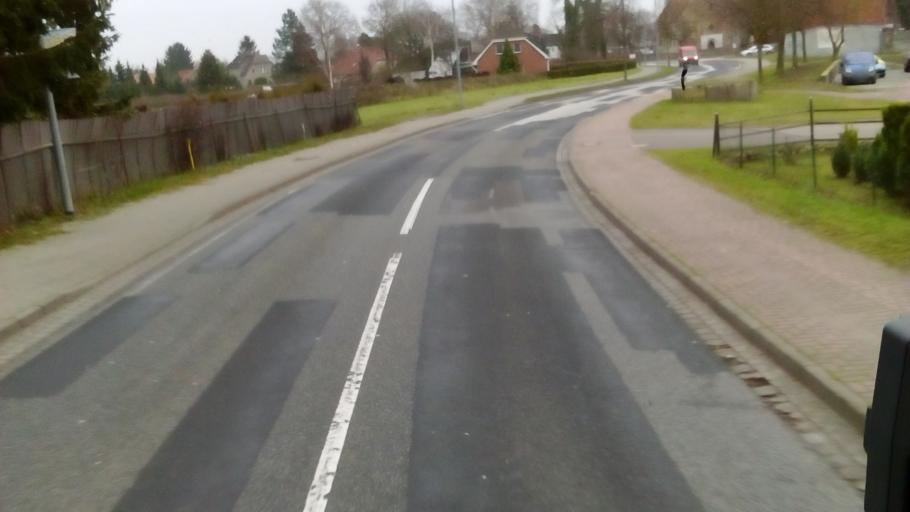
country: DE
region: Mecklenburg-Vorpommern
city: Pasewalk
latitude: 53.4968
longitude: 13.9440
